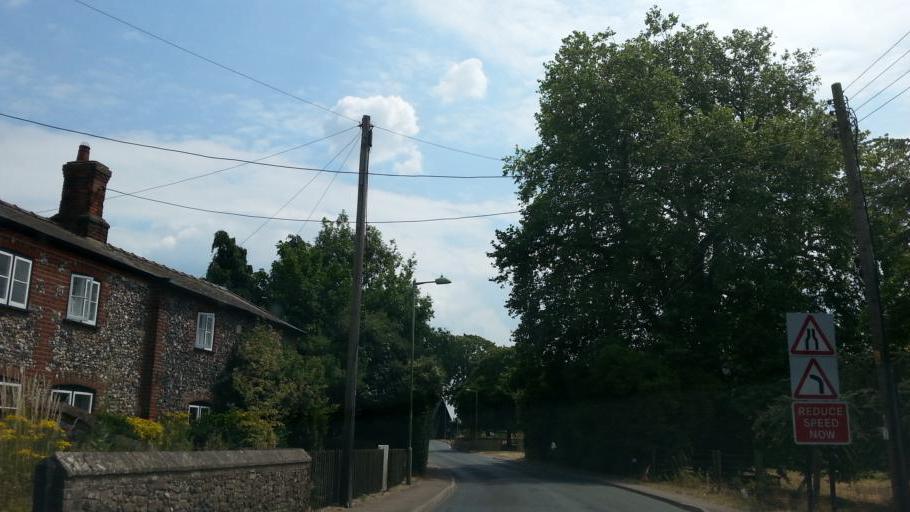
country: GB
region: England
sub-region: Suffolk
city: Lakenheath
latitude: 52.3740
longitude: 0.5299
